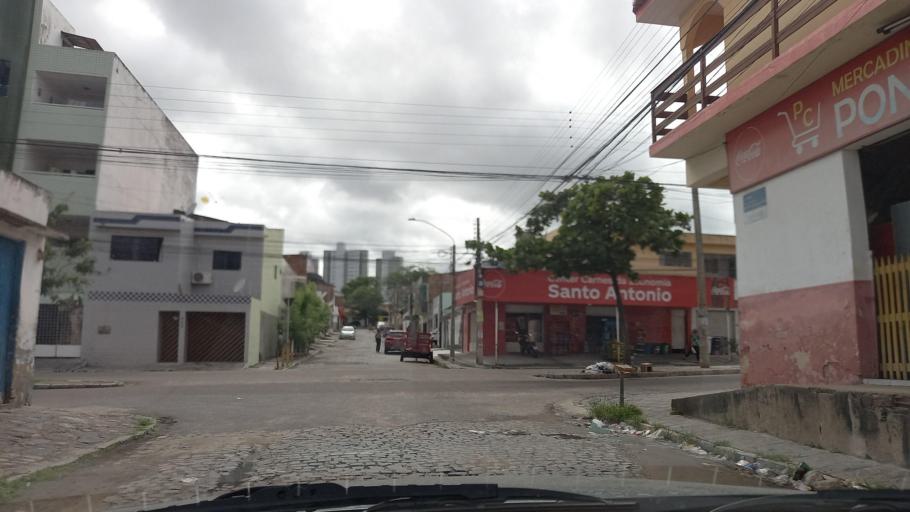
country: BR
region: Pernambuco
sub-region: Caruaru
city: Caruaru
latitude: -8.2778
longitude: -35.9787
